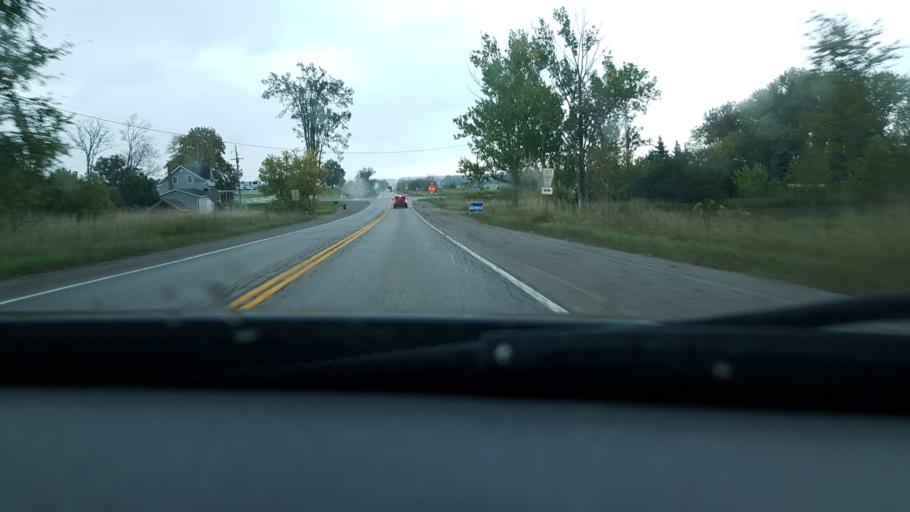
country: CA
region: Ontario
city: Omemee
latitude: 44.3841
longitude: -78.6004
